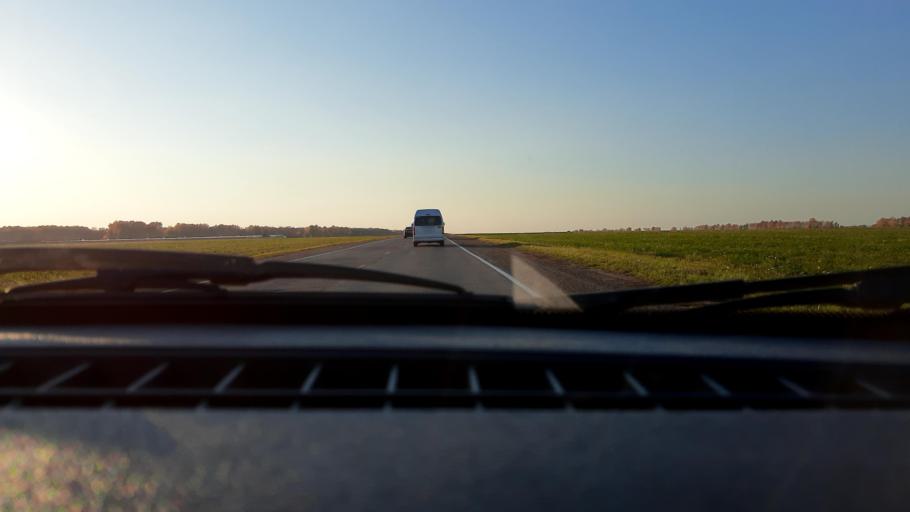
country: RU
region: Bashkortostan
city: Avdon
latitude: 54.8225
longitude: 55.6606
